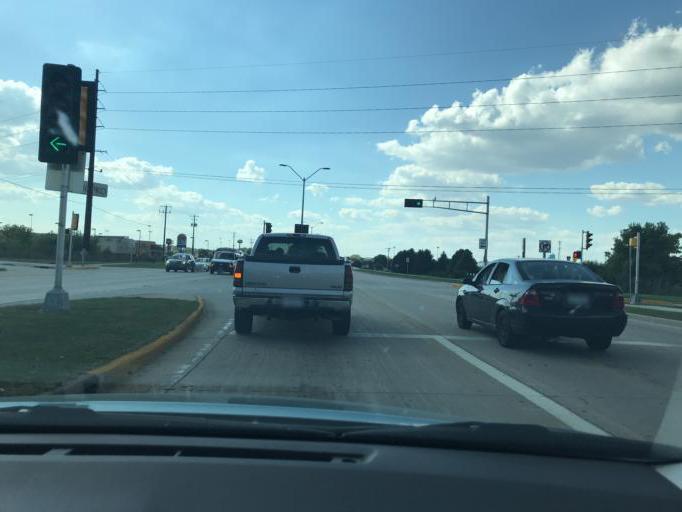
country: US
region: Wisconsin
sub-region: Walworth County
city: Delavan
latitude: 42.6277
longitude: -88.6198
